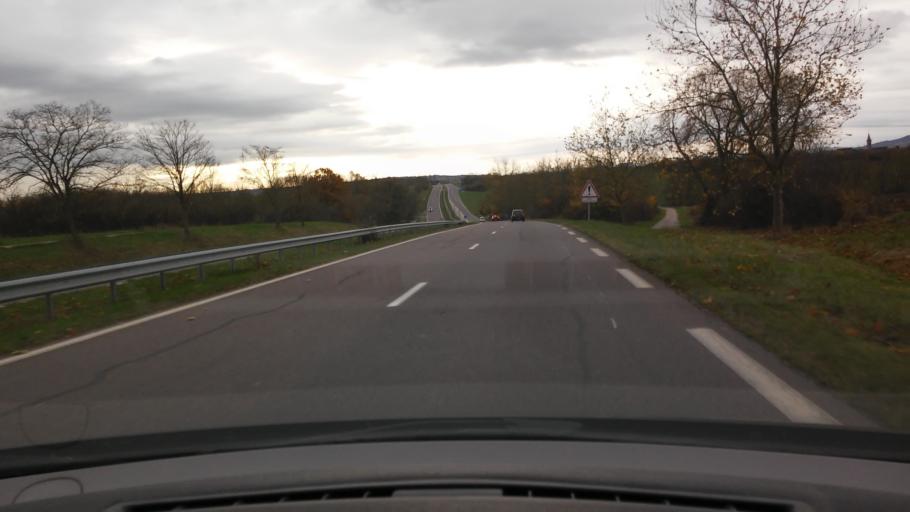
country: FR
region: Lorraine
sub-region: Departement de la Moselle
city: Argancy
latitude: 49.2065
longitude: 6.2090
